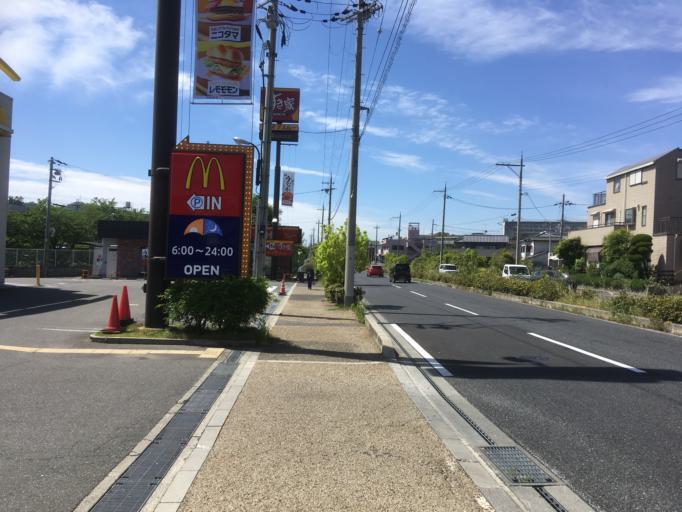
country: JP
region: Nara
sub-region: Ikoma-shi
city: Ikoma
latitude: 34.6696
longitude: 135.7070
